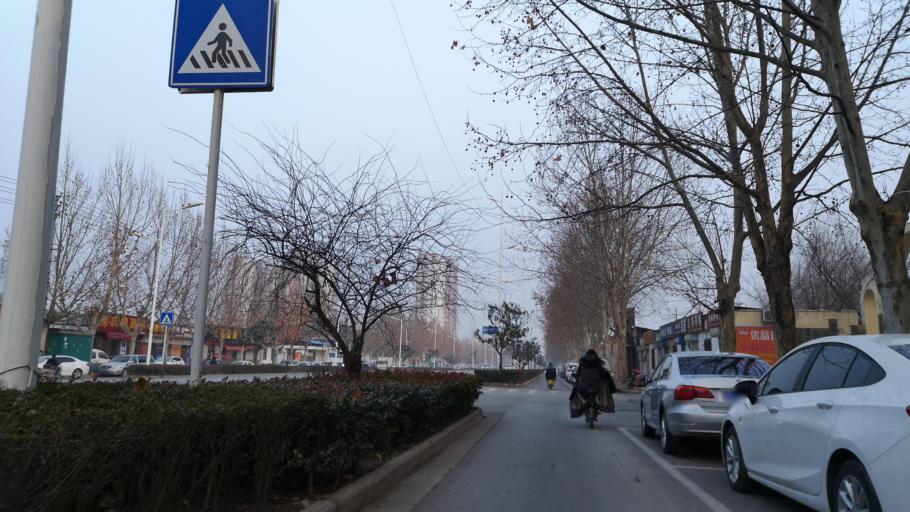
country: CN
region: Henan Sheng
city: Puyang
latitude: 35.7487
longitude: 115.0324
